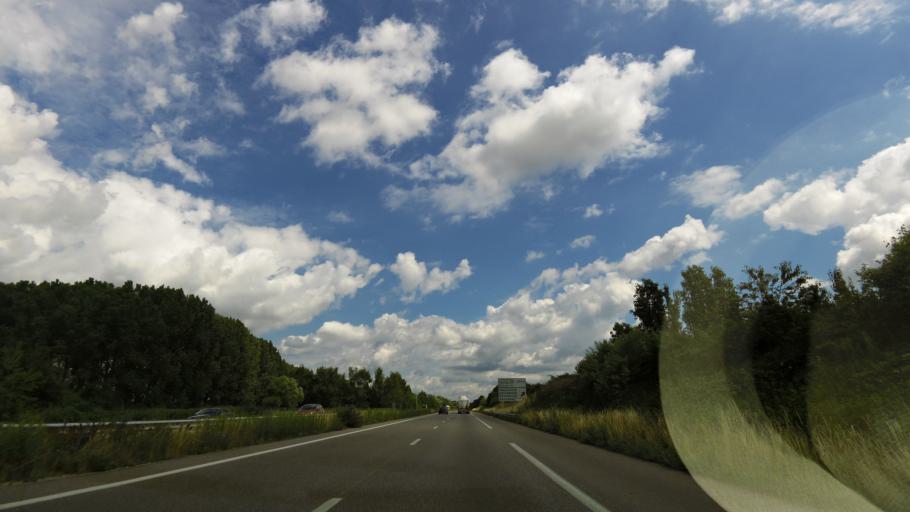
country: FR
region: Alsace
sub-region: Departement du Bas-Rhin
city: Herrlisheim
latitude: 48.7394
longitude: 7.9039
